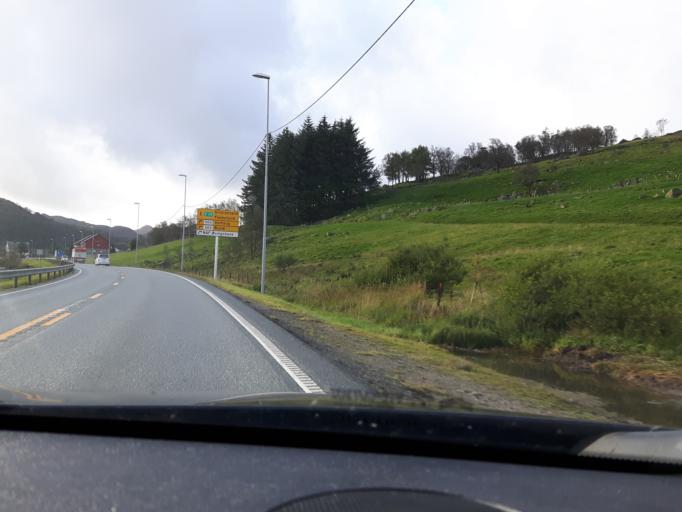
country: NO
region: Rogaland
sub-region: Bjerkreim
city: Vikesa
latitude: 58.6712
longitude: 5.9834
